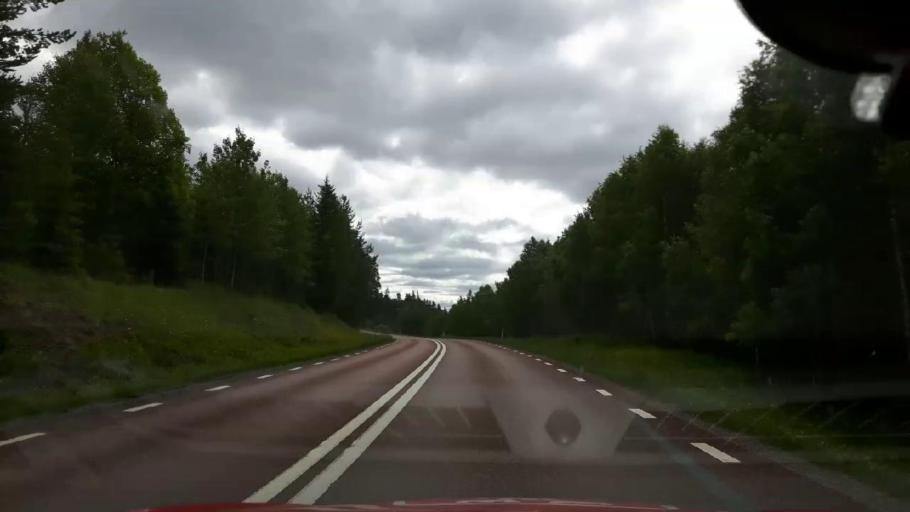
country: SE
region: Jaemtland
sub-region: OEstersunds Kommun
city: Brunflo
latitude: 62.9488
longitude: 15.0531
